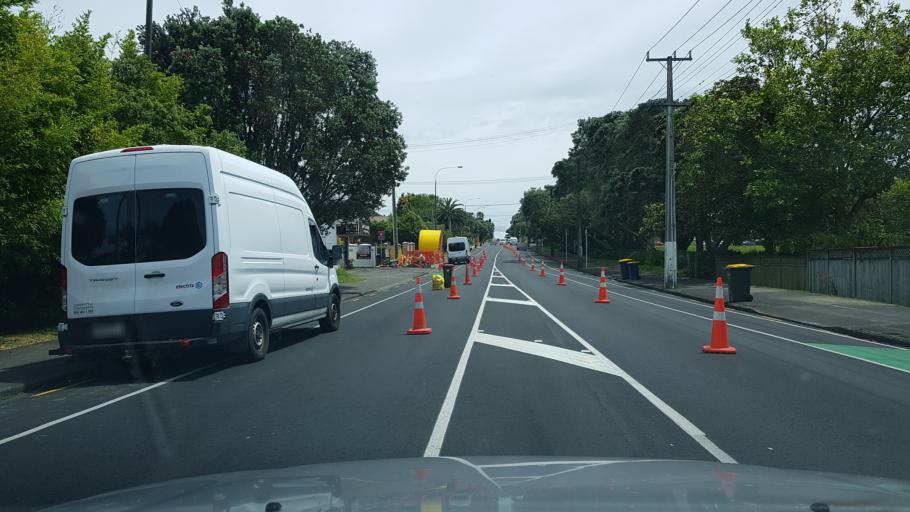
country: NZ
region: Auckland
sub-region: Auckland
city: North Shore
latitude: -36.8031
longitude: 174.7877
